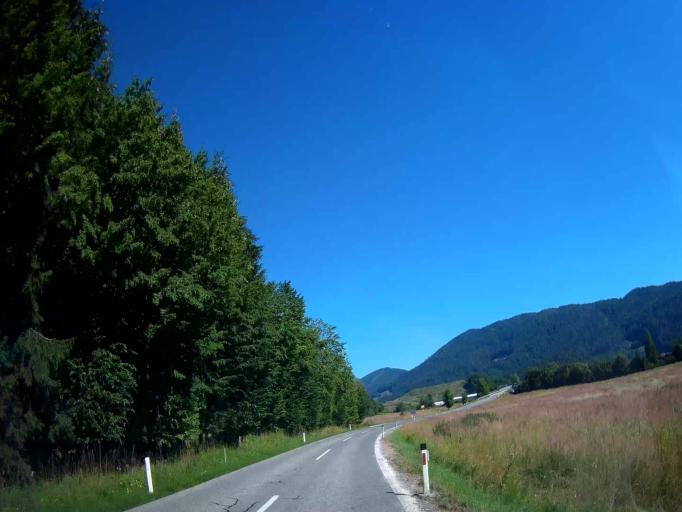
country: AT
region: Carinthia
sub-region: Politischer Bezirk Volkermarkt
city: Voelkermarkt
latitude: 46.6436
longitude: 14.5482
